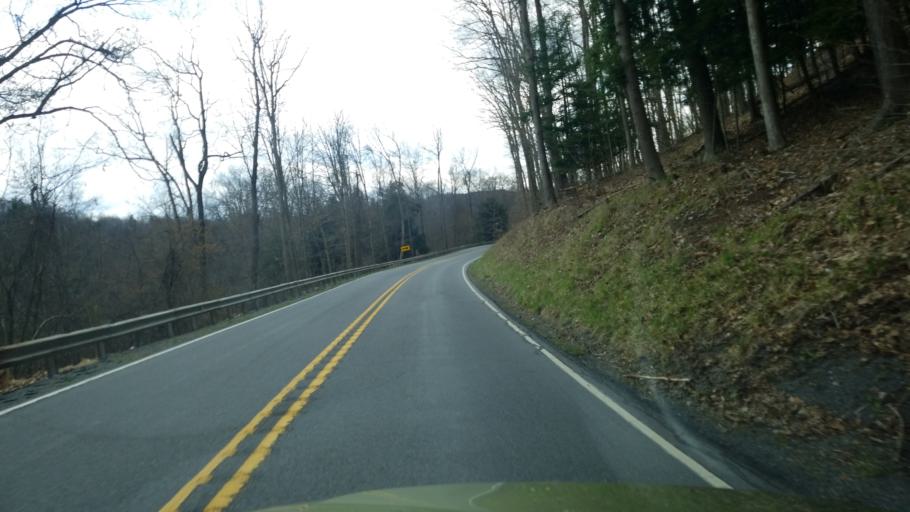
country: US
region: Pennsylvania
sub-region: Clearfield County
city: Curwensville
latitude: 40.8387
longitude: -78.4424
